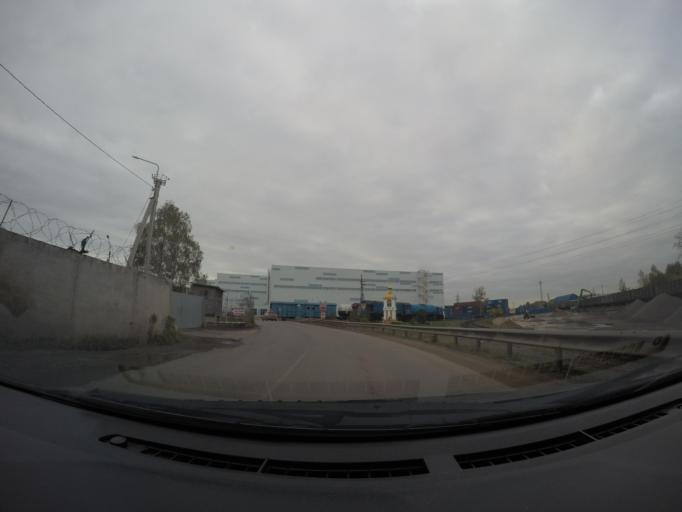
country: RU
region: Moskovskaya
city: Staraya Kupavna
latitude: 55.7913
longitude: 38.1838
